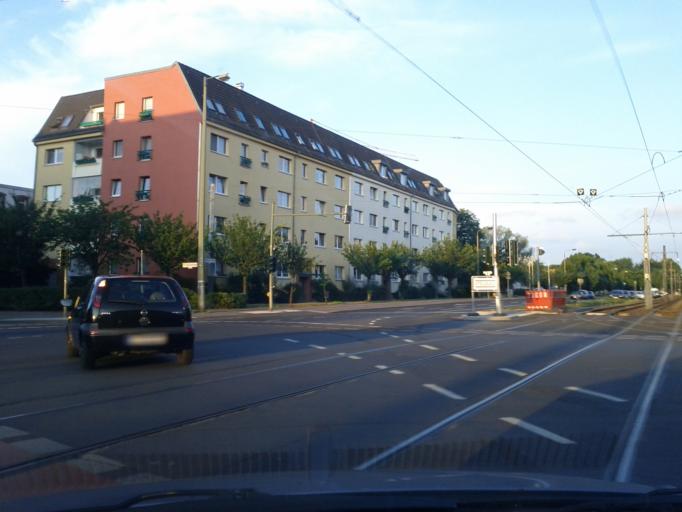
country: DE
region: Berlin
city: Berlin Koepenick
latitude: 52.4426
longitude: 13.5821
